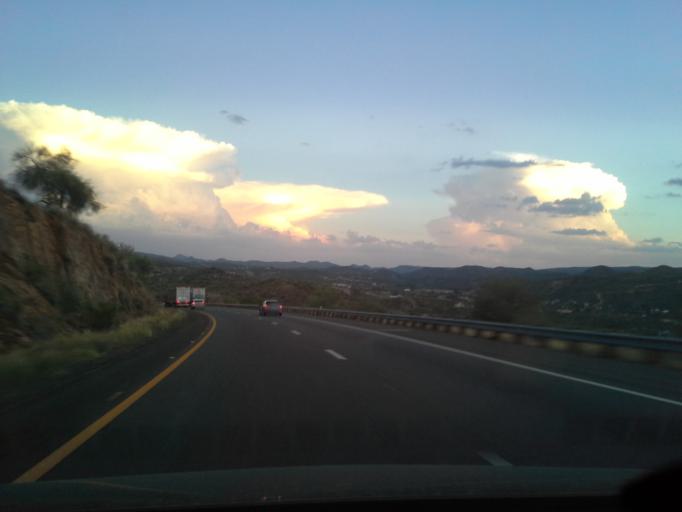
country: US
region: Arizona
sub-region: Yavapai County
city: Black Canyon City
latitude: 34.1073
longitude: -112.1437
